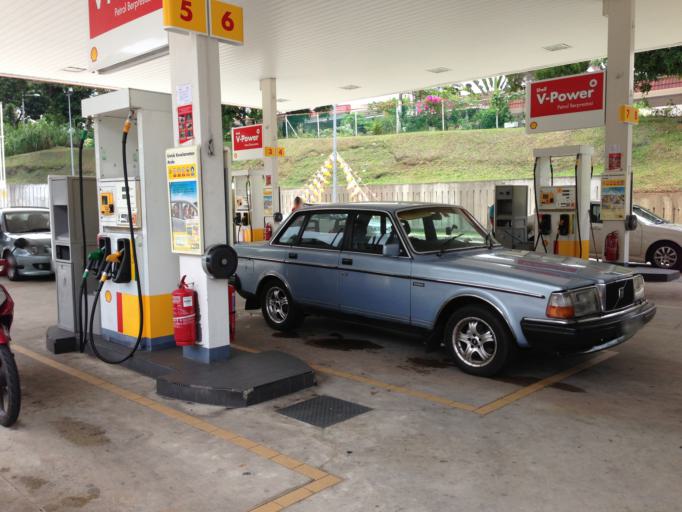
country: MY
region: Melaka
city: Kampung Ayer Keroh
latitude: 2.2495
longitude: 102.2917
